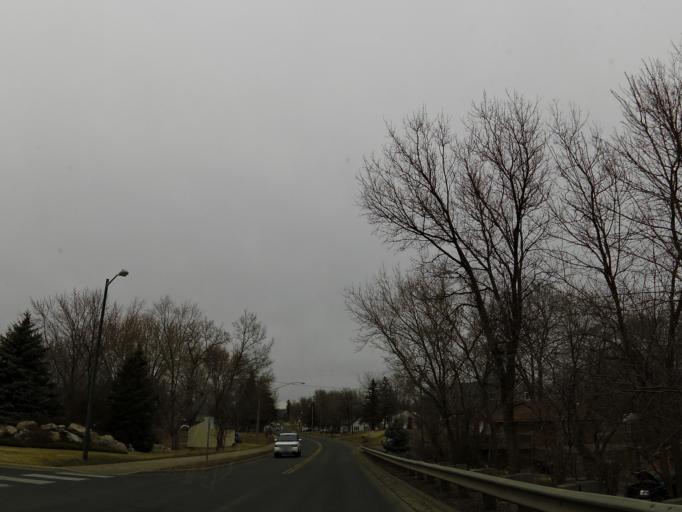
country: US
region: Minnesota
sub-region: Scott County
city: Prior Lake
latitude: 44.7095
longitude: -93.4296
